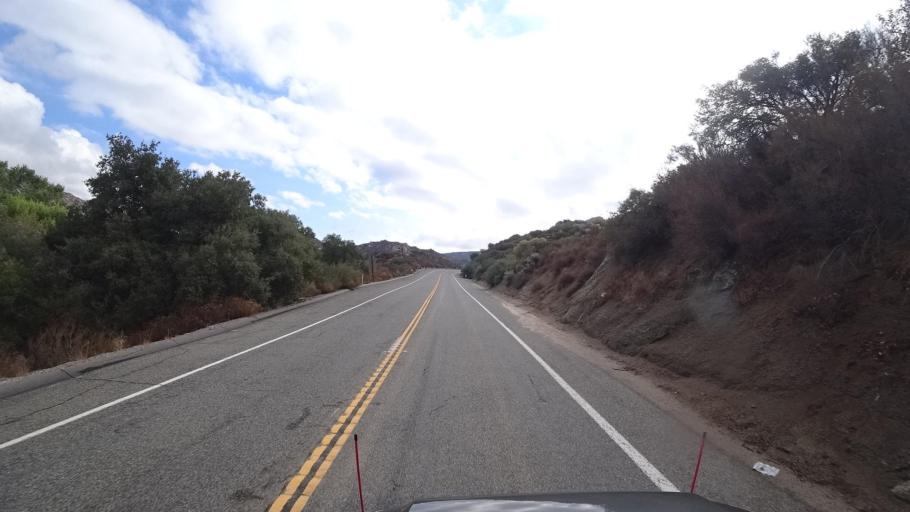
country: MX
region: Baja California
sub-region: Tecate
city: Hacienda Tecate
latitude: 32.5908
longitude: -116.5253
